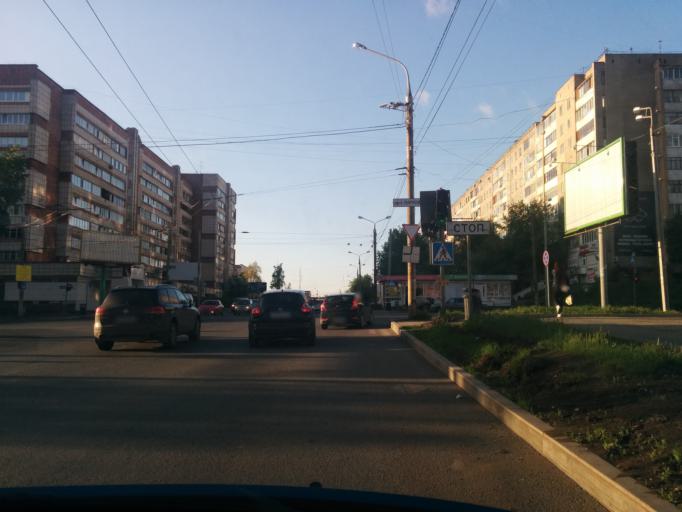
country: RU
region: Perm
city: Kondratovo
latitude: 57.9976
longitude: 56.1672
